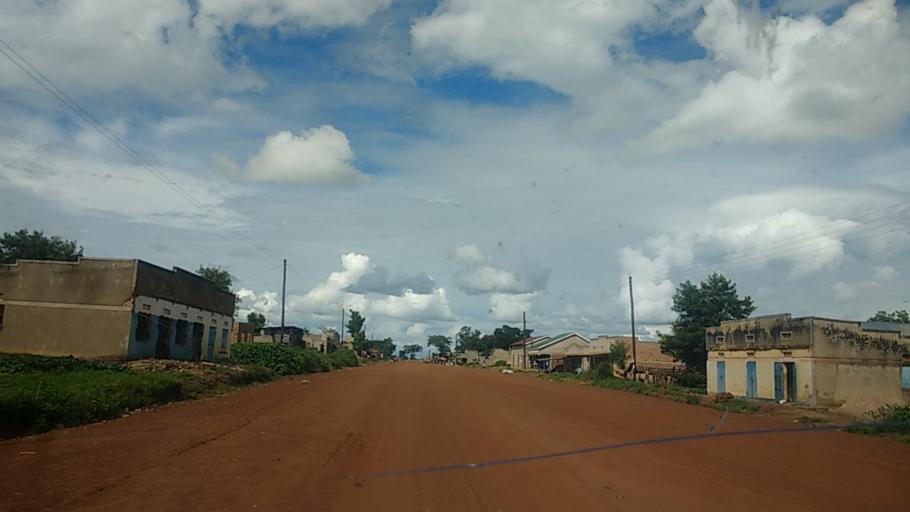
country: UG
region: Eastern Region
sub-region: Katakwi District
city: Katakwi
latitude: 1.9196
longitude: 33.9849
